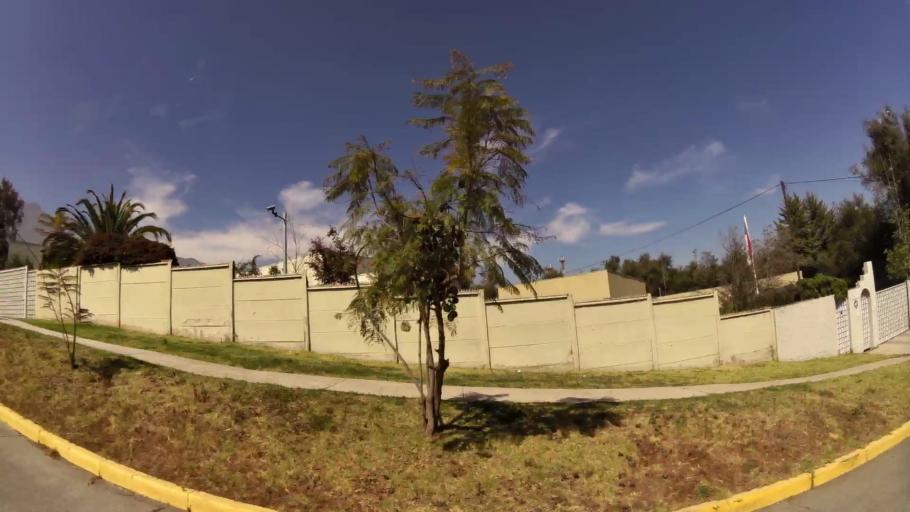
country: CL
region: Santiago Metropolitan
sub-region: Provincia de Santiago
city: Villa Presidente Frei, Nunoa, Santiago, Chile
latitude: -33.4594
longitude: -70.5270
